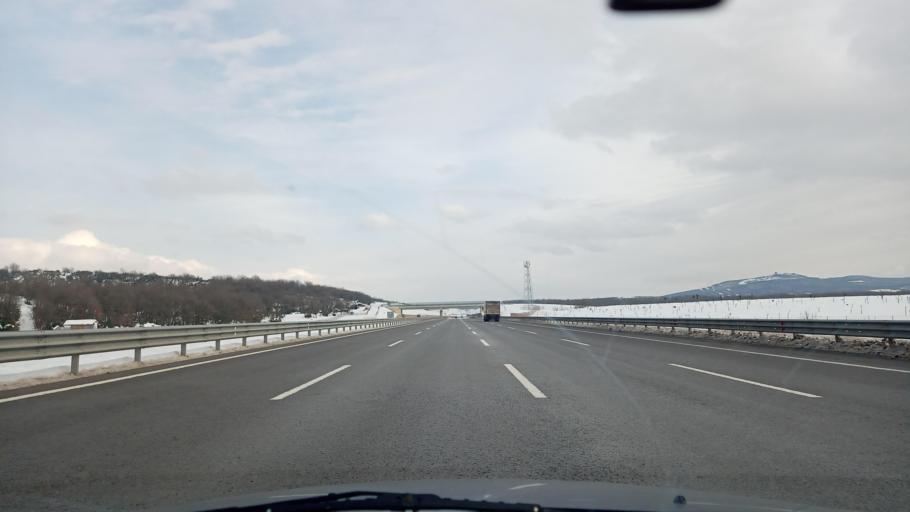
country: TR
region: Kocaeli
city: Mollafeneri
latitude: 40.8895
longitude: 29.5902
